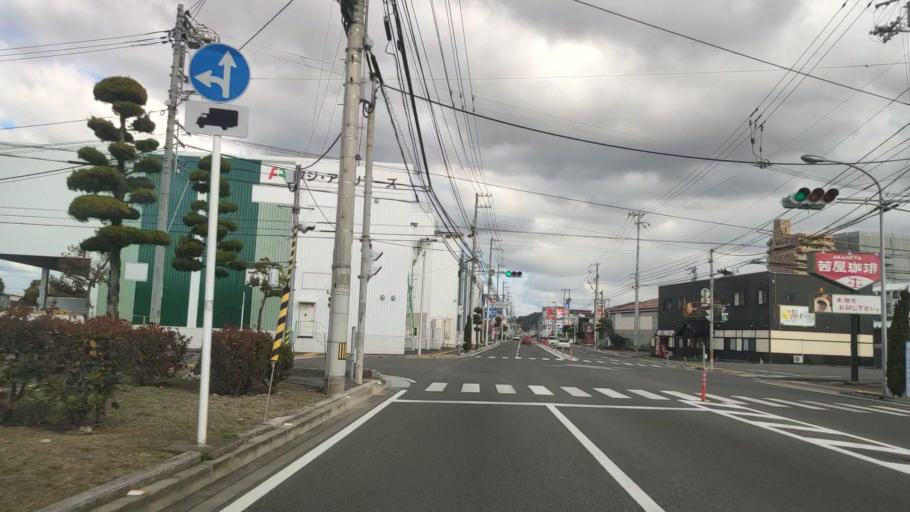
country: JP
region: Ehime
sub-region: Shikoku-chuo Shi
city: Matsuyama
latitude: 33.8607
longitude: 132.7493
